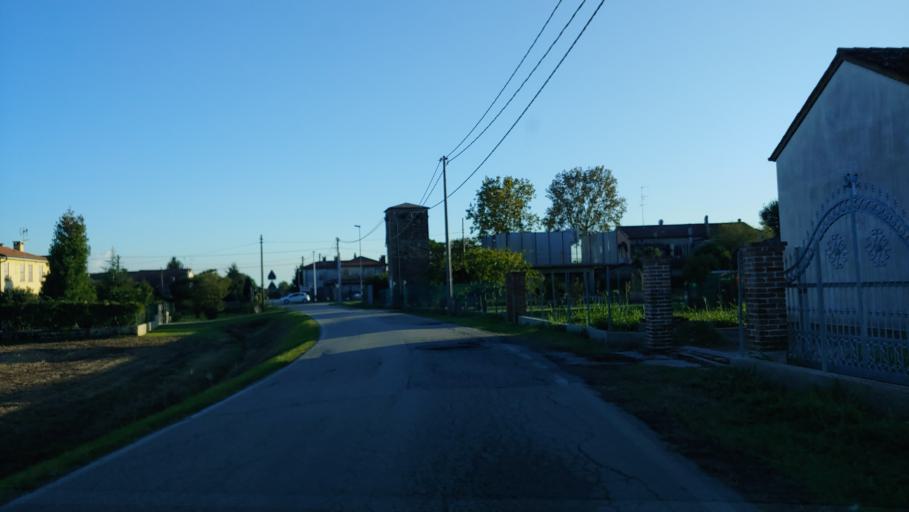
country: IT
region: Veneto
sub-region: Provincia di Rovigo
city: Pettorazza Grimani
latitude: 45.0654
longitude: 11.9831
